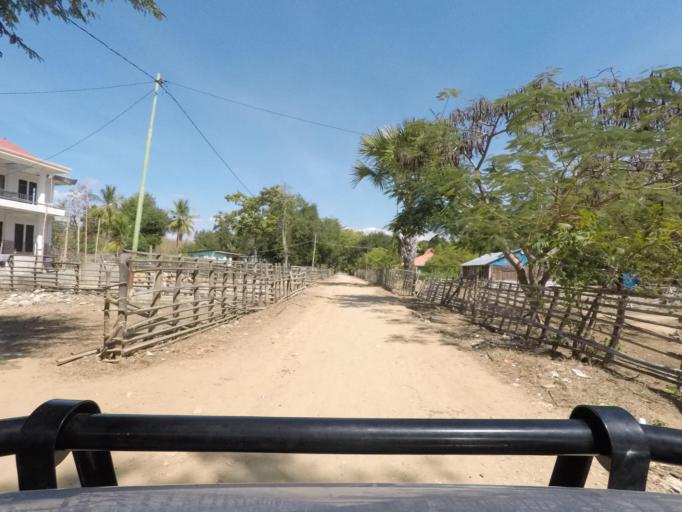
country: TL
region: Liquica
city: Maubara
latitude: -8.7835
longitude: 125.1037
